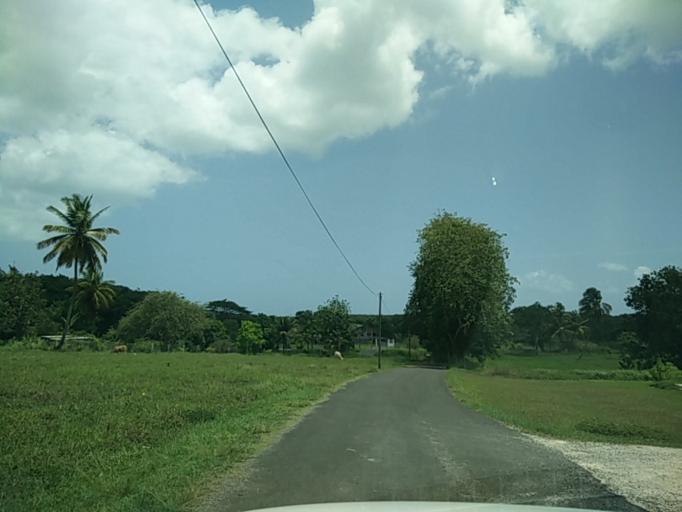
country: GP
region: Guadeloupe
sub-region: Guadeloupe
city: Les Abymes
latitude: 16.2893
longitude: -61.5235
